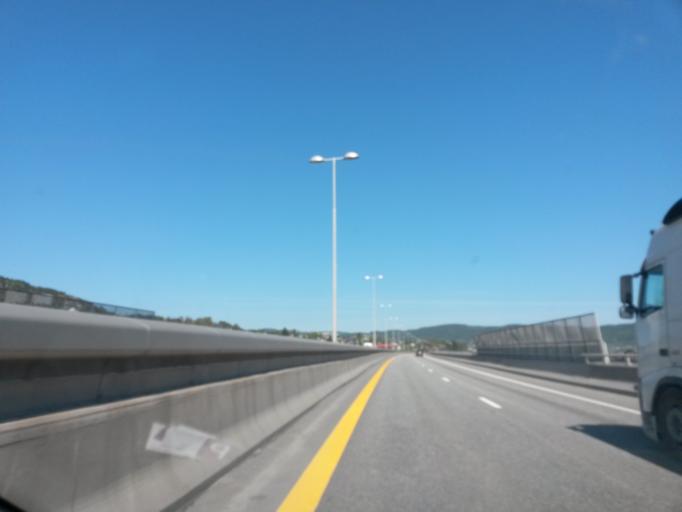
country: NO
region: Buskerud
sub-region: Drammen
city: Drammen
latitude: 59.7373
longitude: 10.2203
